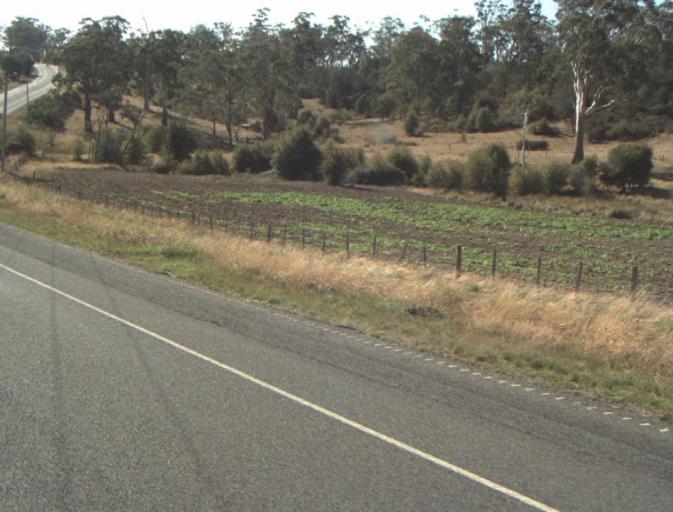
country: AU
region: Tasmania
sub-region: Launceston
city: Mayfield
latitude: -41.3497
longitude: 147.0972
